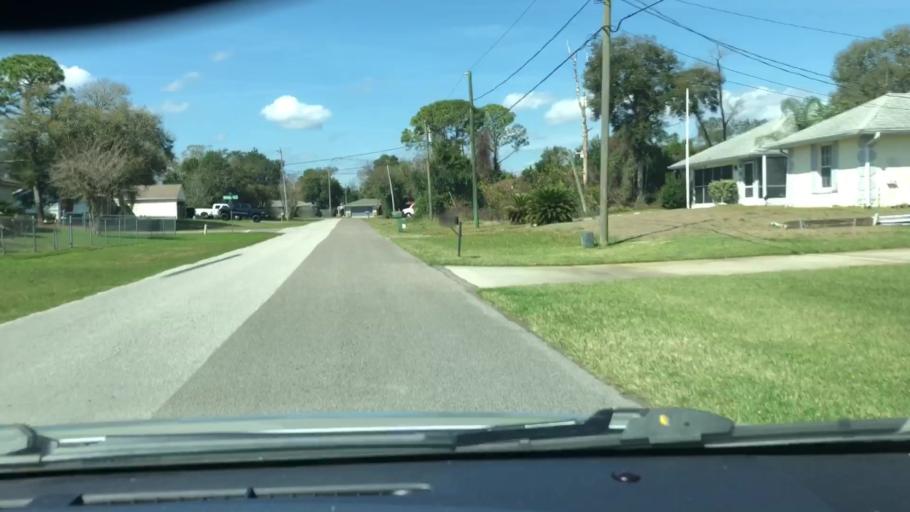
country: US
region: Florida
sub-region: Volusia County
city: Deltona
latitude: 28.8884
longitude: -81.2310
